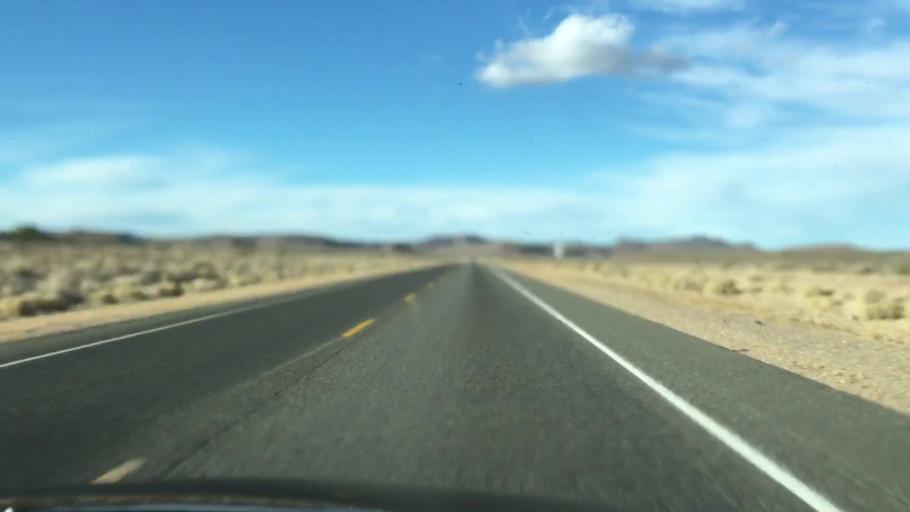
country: US
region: Nevada
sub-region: Esmeralda County
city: Goldfield
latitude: 37.5980
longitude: -117.2113
